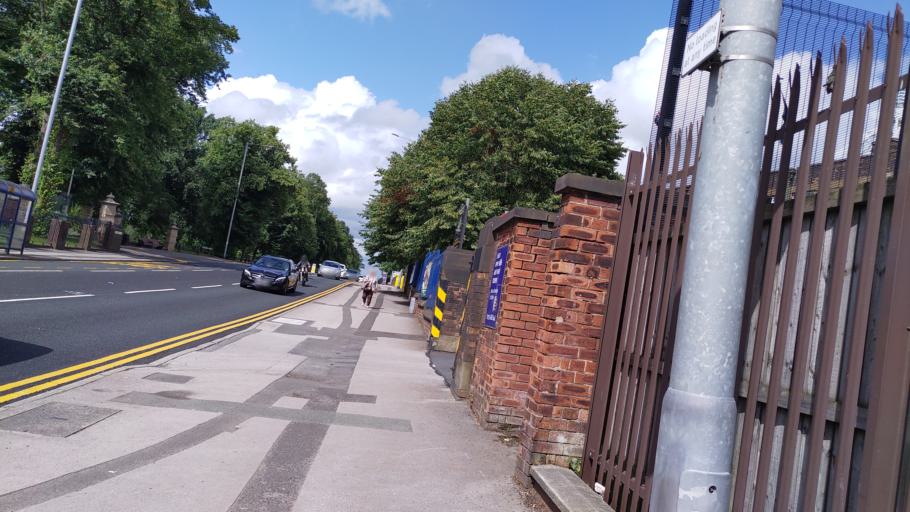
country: GB
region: England
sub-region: Lancashire
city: Preston
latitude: 53.7708
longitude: -2.6907
